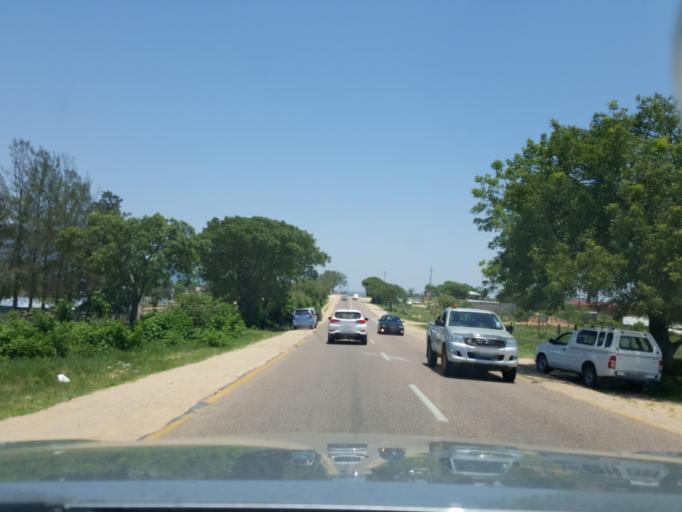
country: ZA
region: Limpopo
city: Thulamahashi
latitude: -24.5935
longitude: 31.0437
